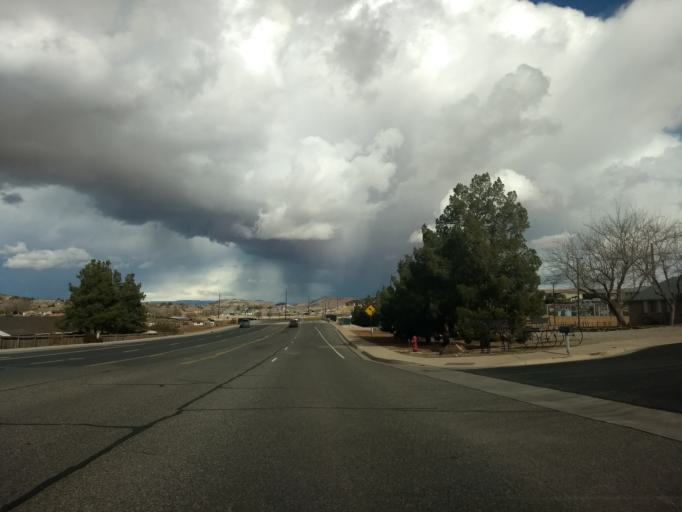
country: US
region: Utah
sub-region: Washington County
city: Saint George
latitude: 37.0583
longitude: -113.5476
